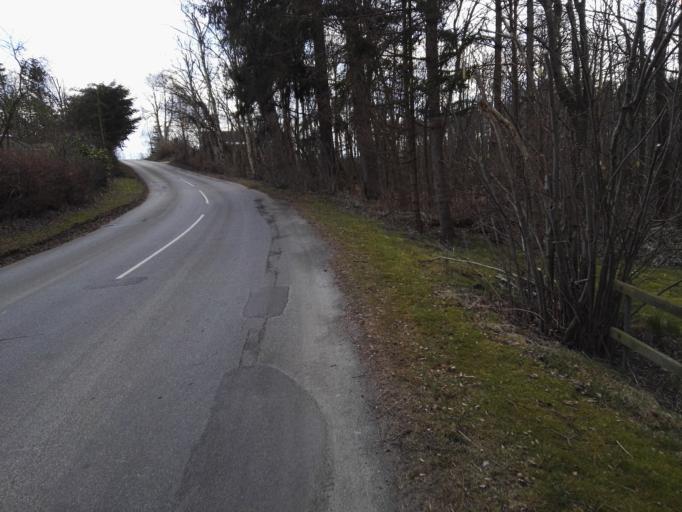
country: DK
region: Zealand
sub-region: Lejre Kommune
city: Ejby
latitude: 55.7625
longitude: 11.8206
